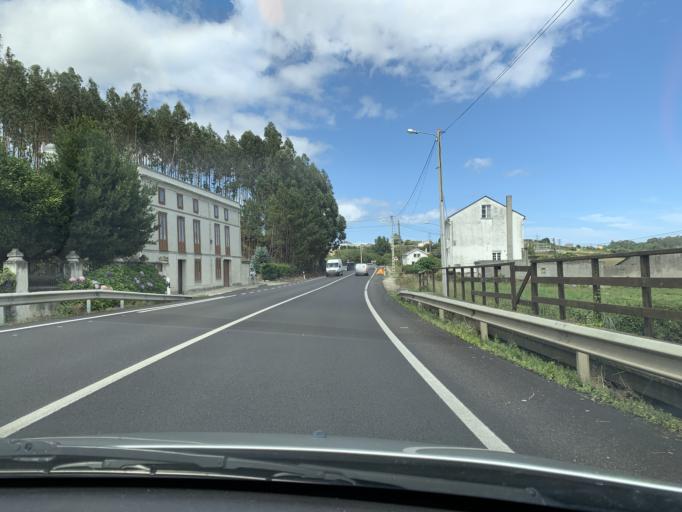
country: ES
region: Galicia
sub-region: Provincia de Lugo
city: Foz
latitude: 43.5426
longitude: -7.2699
